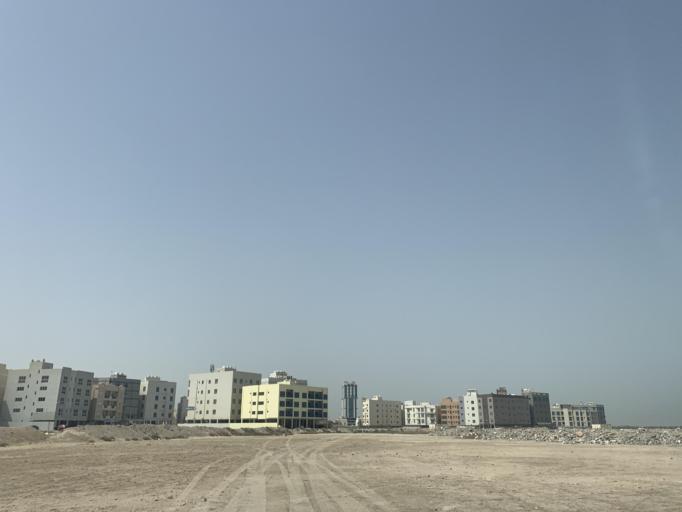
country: BH
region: Manama
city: Jidd Hafs
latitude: 26.2429
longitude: 50.5299
